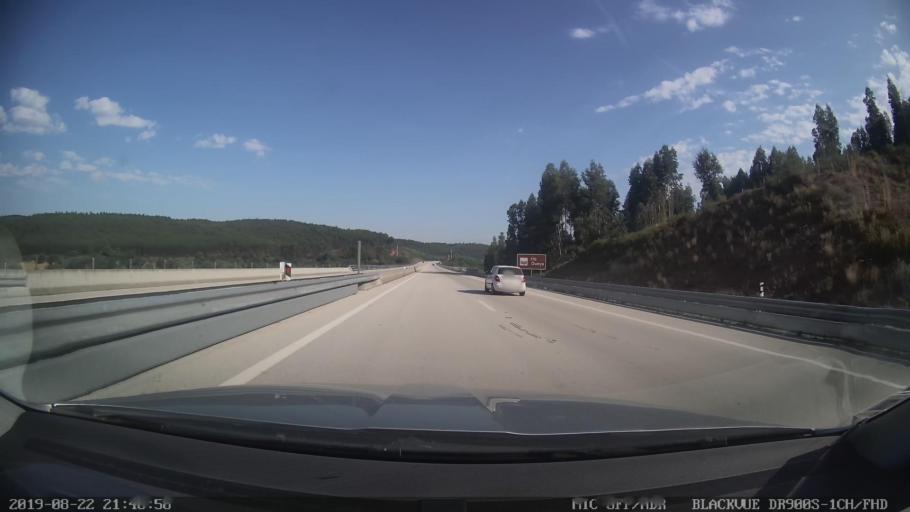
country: PT
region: Coimbra
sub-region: Penela
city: Penela
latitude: 40.0356
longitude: -8.3720
